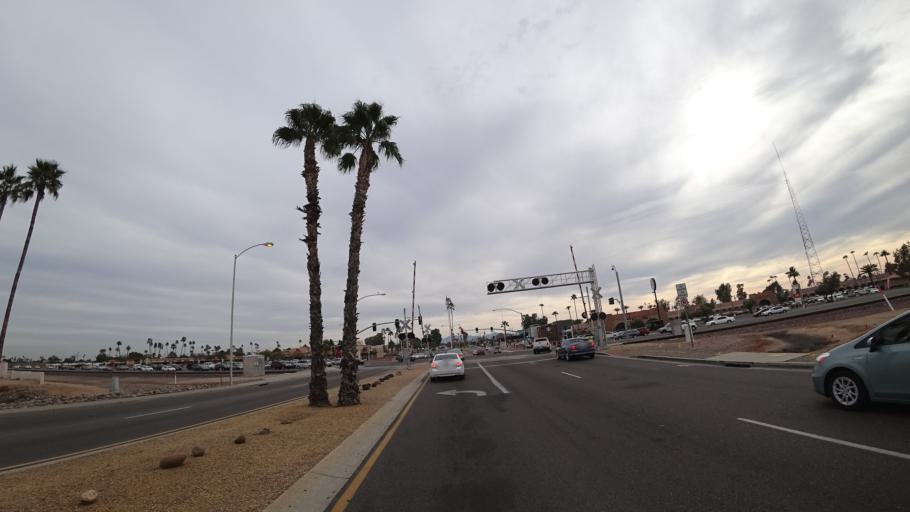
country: US
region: Arizona
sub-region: Maricopa County
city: Youngtown
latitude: 33.6033
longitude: -112.2900
